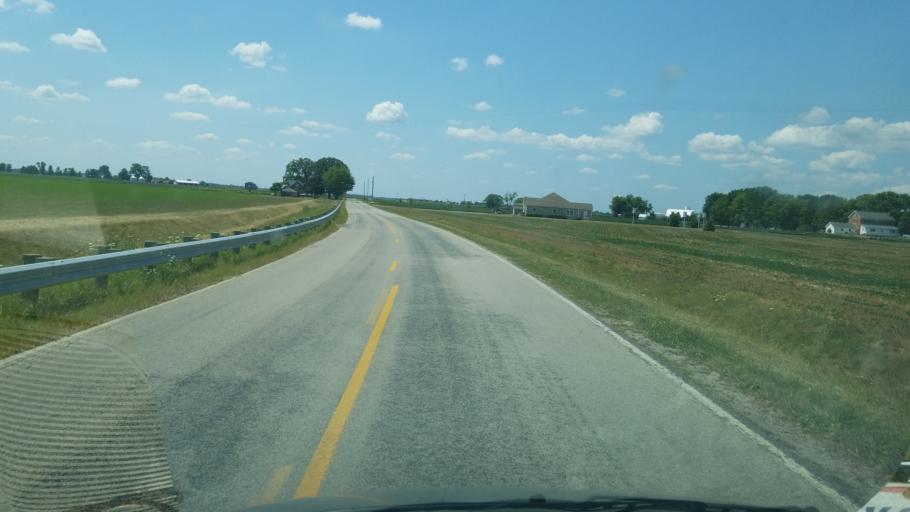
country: US
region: Ohio
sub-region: Madison County
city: Plain City
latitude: 40.0447
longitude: -83.3458
